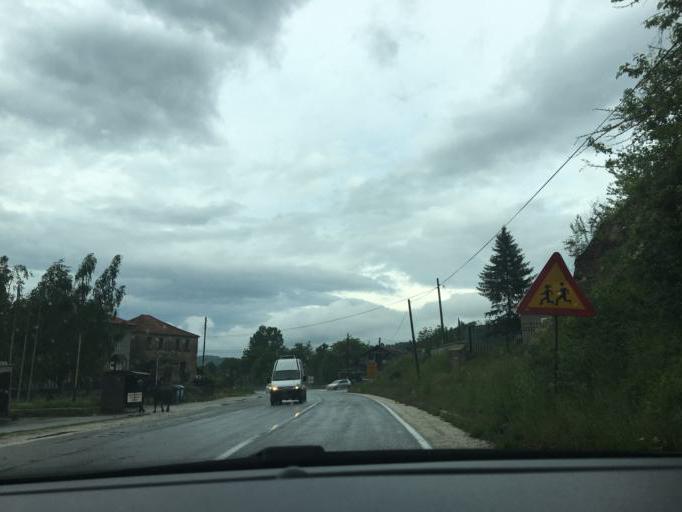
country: MK
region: Debarca
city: Belcista
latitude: 41.2846
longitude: 20.7906
